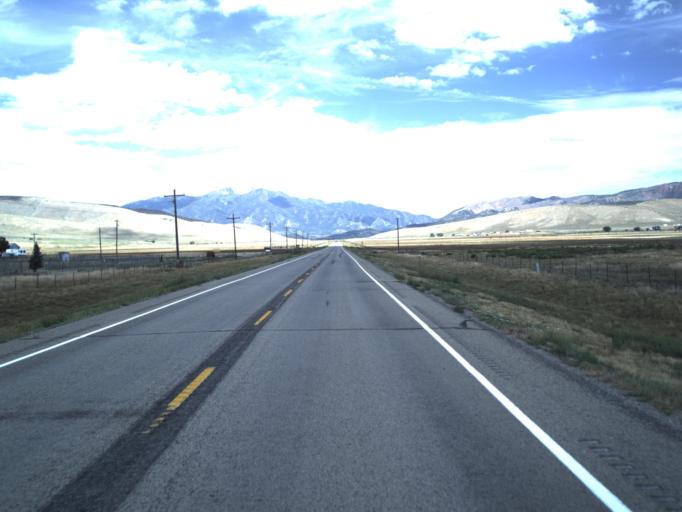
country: US
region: Utah
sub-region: Sanpete County
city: Fairview
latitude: 39.7771
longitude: -111.4904
